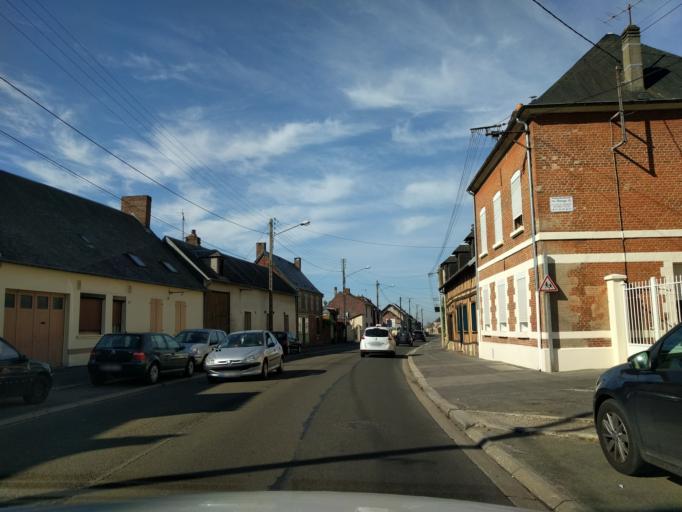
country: FR
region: Picardie
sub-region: Departement de l'Oise
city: Breteuil
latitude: 49.5667
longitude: 2.2215
